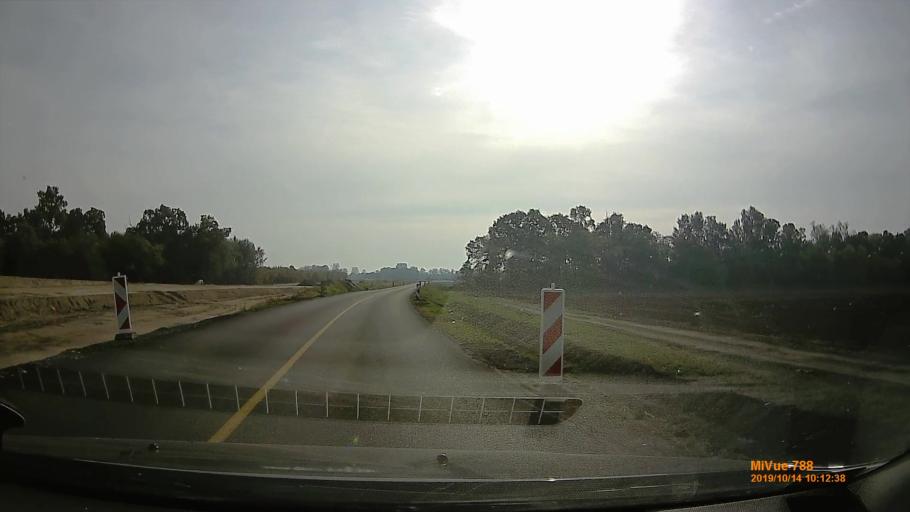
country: HU
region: Pest
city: Tortel
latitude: 47.1909
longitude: 19.9201
